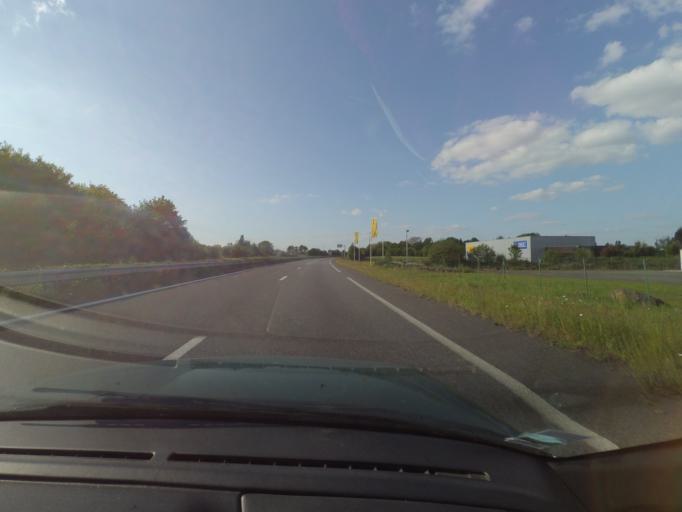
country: FR
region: Pays de la Loire
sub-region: Departement de la Vendee
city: Saligny
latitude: 46.8038
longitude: -1.4325
